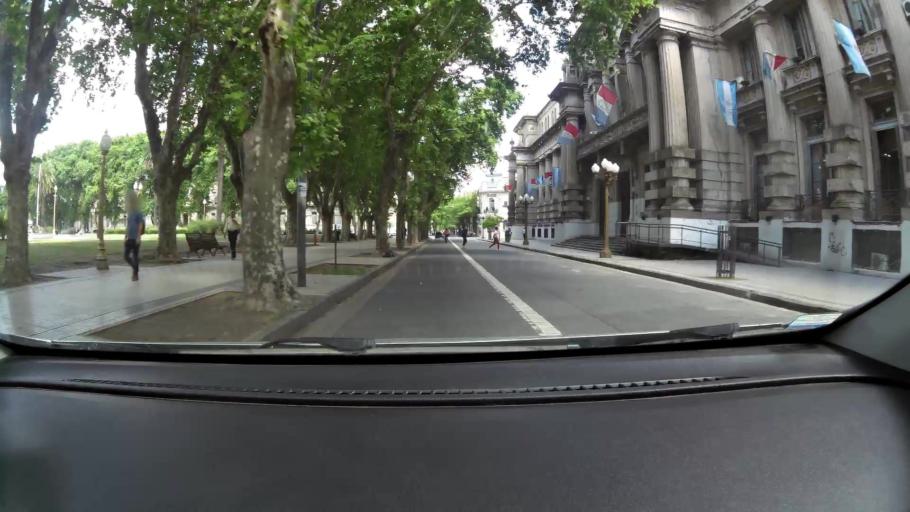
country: AR
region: Santa Fe
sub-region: Departamento de Rosario
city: Rosario
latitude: -32.9431
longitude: -60.6493
